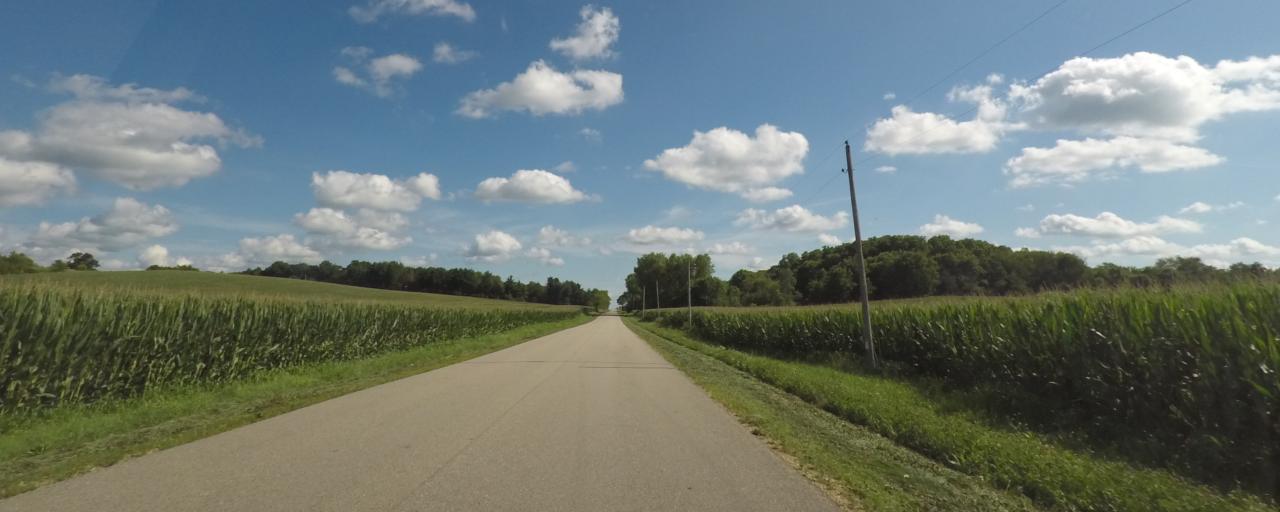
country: US
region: Wisconsin
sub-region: Dane County
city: Stoughton
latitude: 42.9072
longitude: -89.1319
